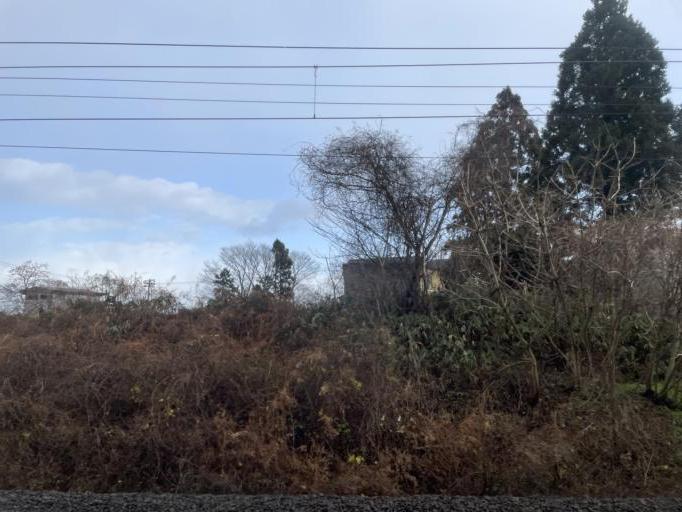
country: JP
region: Aomori
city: Aomori Shi
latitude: 40.9234
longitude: 141.0217
